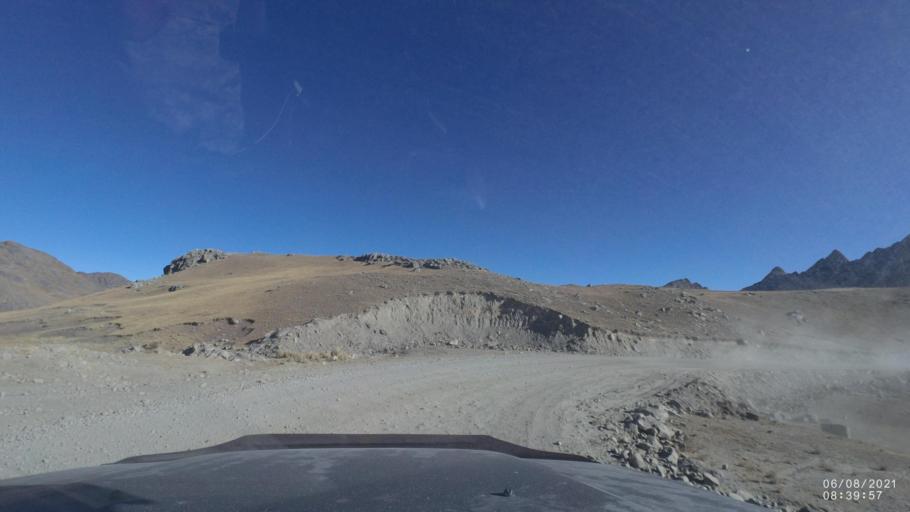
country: BO
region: Cochabamba
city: Sipe Sipe
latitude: -17.1748
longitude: -66.4010
